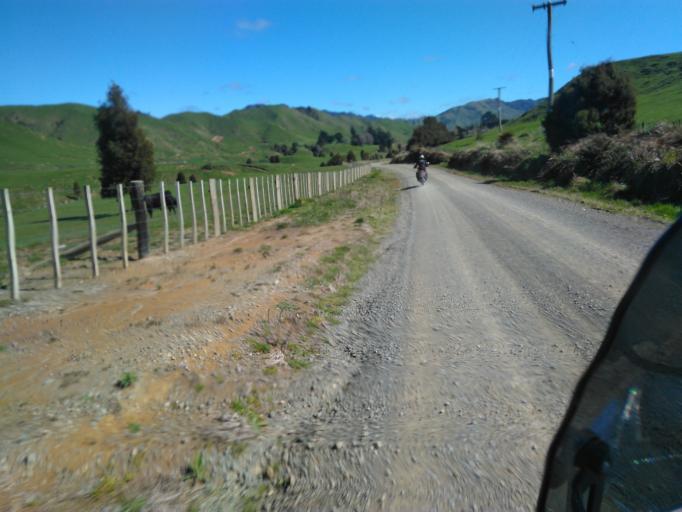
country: NZ
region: Bay of Plenty
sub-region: Opotiki District
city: Opotiki
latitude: -38.3017
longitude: 177.5600
